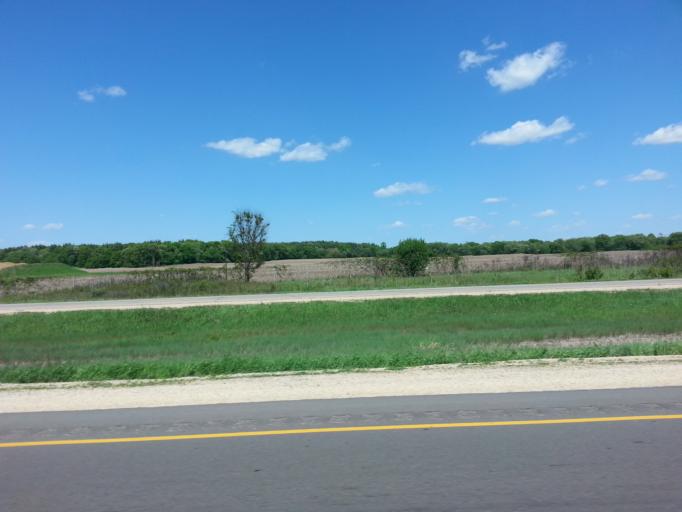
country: US
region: Wisconsin
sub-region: Rock County
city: Janesville
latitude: 42.7337
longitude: -89.0028
